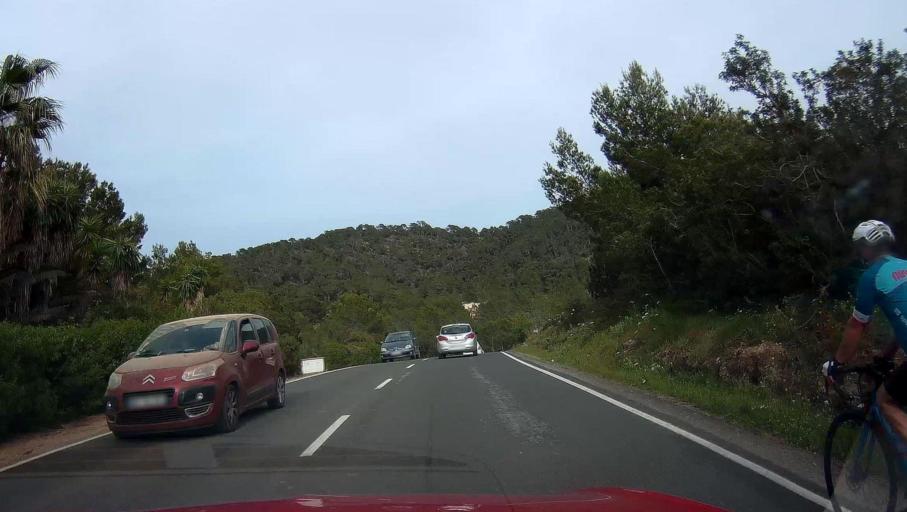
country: ES
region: Balearic Islands
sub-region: Illes Balears
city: Sant Joan de Labritja
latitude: 39.1001
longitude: 1.5078
